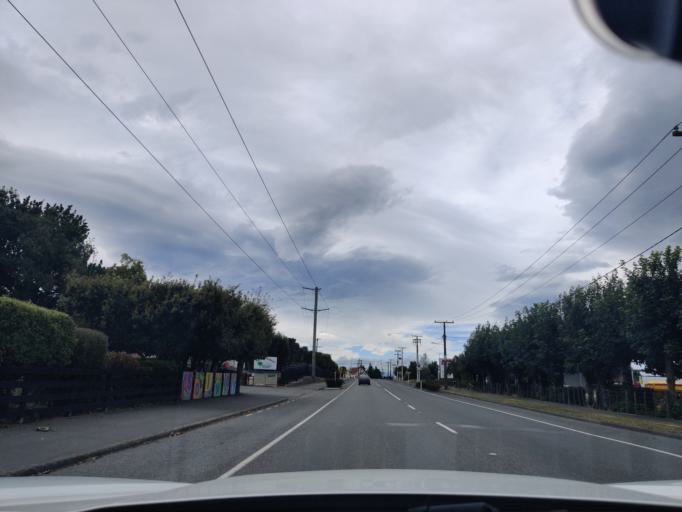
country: NZ
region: Wellington
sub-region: Masterton District
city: Masterton
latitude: -40.9608
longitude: 175.6132
